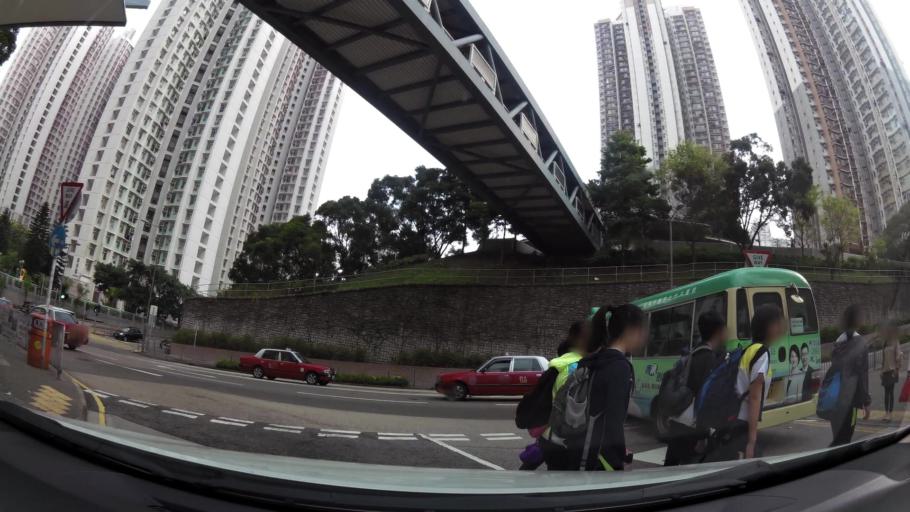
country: HK
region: Kowloon City
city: Kowloon
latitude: 22.3098
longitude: 114.2355
